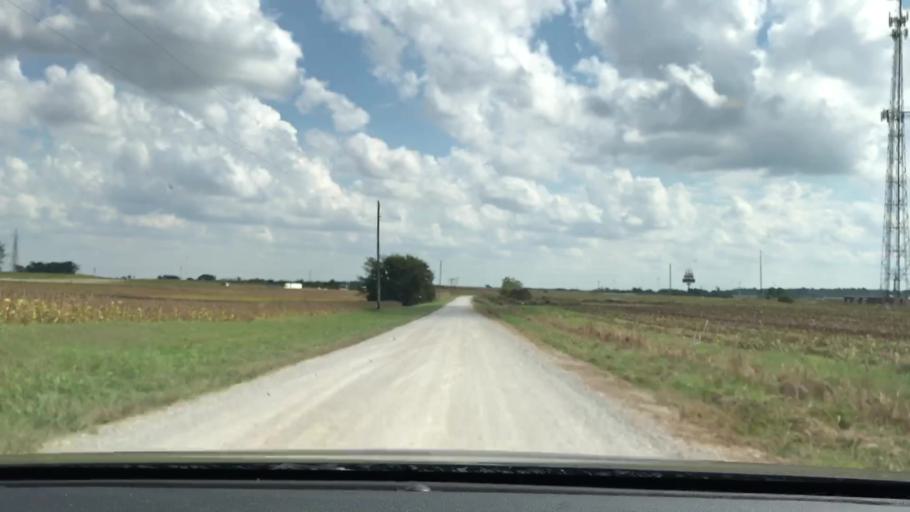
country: US
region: Kentucky
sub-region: Christian County
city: Oak Grove
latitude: 36.6832
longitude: -87.4119
